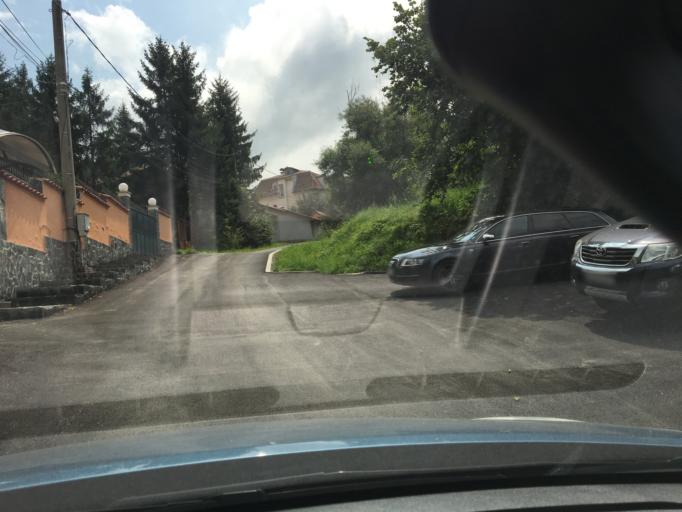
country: BG
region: Sofia-Capital
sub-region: Stolichna Obshtina
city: Sofia
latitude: 42.6100
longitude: 23.3648
